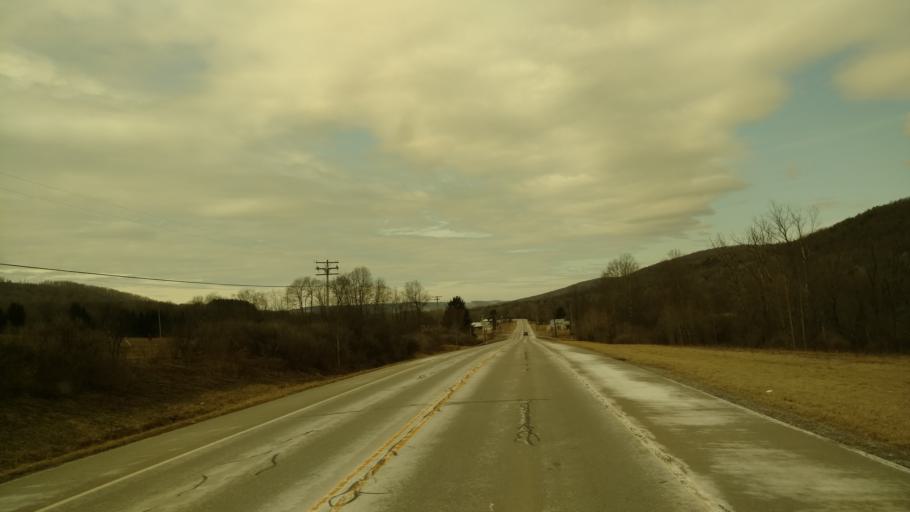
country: US
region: New York
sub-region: Allegany County
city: Wellsville
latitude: 42.0047
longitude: -77.8864
